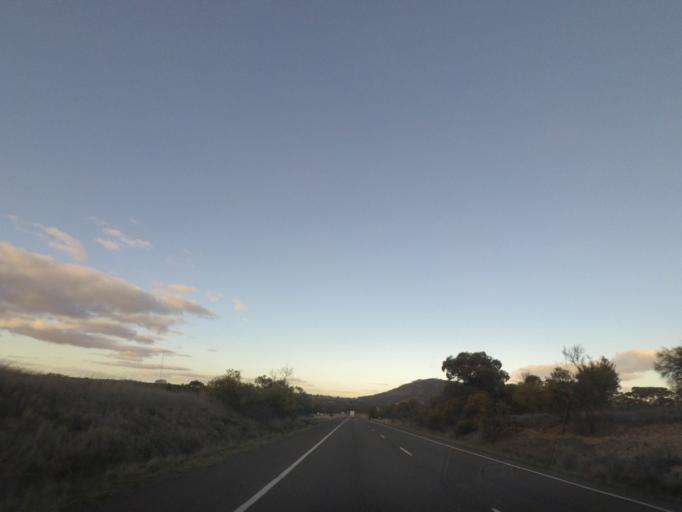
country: AU
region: New South Wales
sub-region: Yass Valley
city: Yass
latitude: -34.7702
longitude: 148.7962
